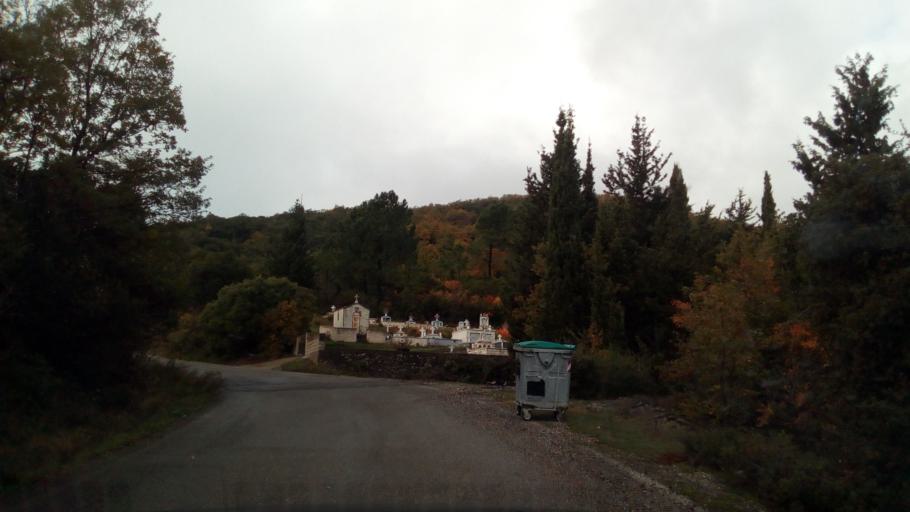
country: GR
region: West Greece
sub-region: Nomos Aitolias kai Akarnanias
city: Nafpaktos
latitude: 38.5216
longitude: 21.9783
